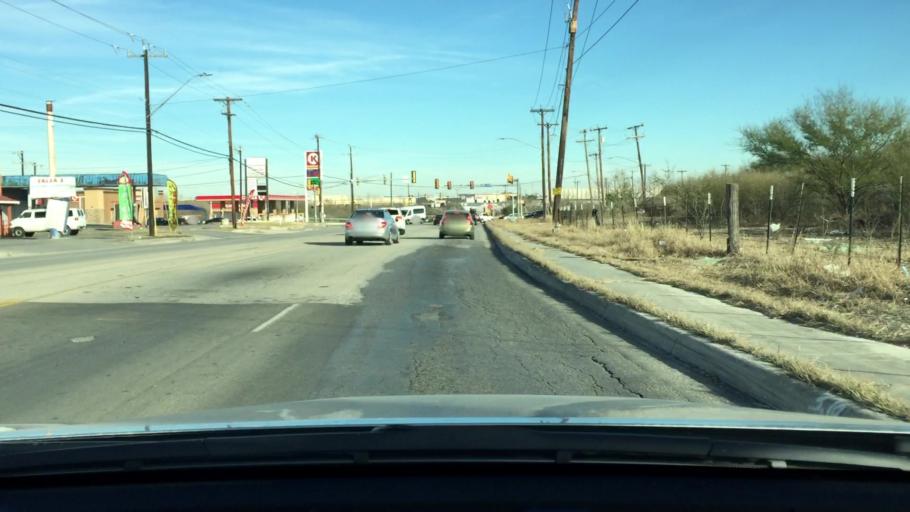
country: US
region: Texas
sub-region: Bexar County
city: Kirby
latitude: 29.4841
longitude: -98.3732
